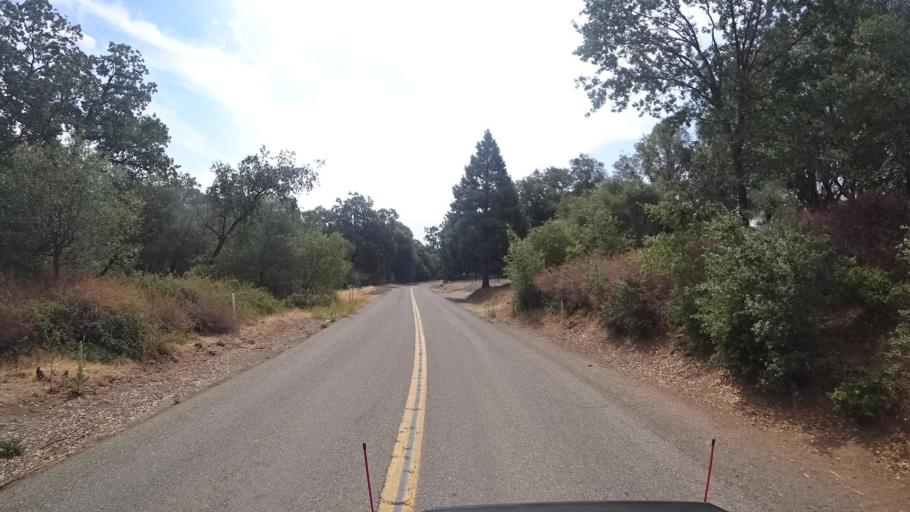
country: US
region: California
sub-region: Mariposa County
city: Midpines
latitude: 37.5082
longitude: -119.8990
